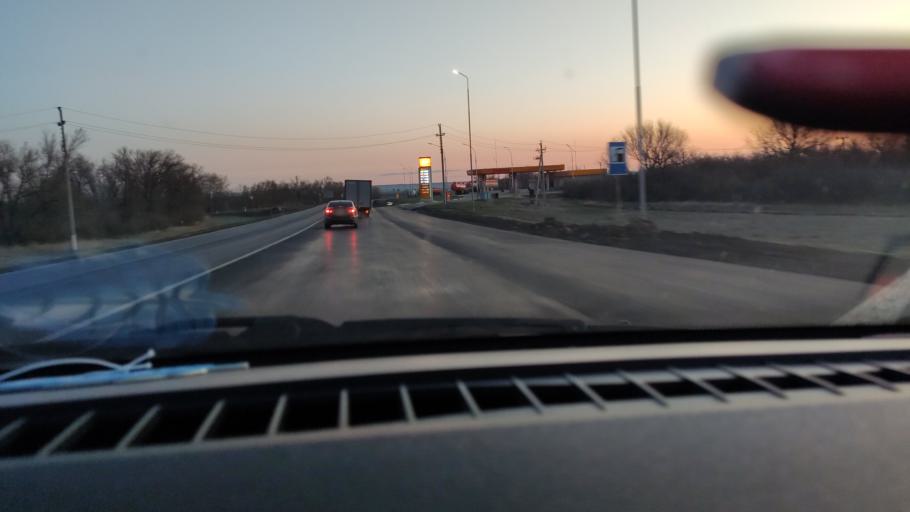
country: RU
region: Saratov
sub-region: Saratovskiy Rayon
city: Saratov
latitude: 51.6800
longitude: 46.0014
